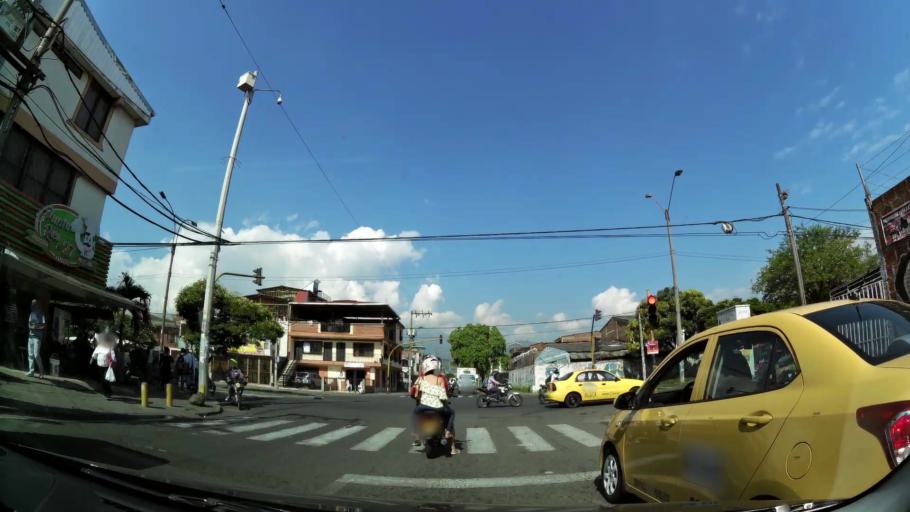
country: CO
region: Valle del Cauca
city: Cali
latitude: 3.4252
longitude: -76.5168
